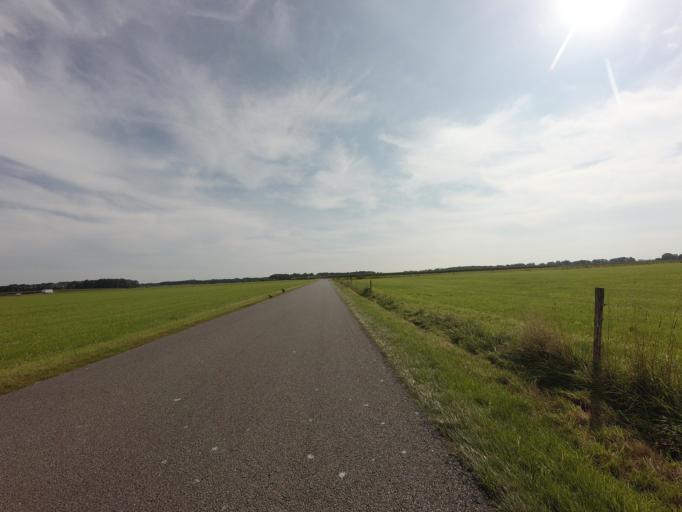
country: NL
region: Drenthe
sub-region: Gemeente Coevorden
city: Dalen
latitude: 52.7172
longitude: 6.7392
